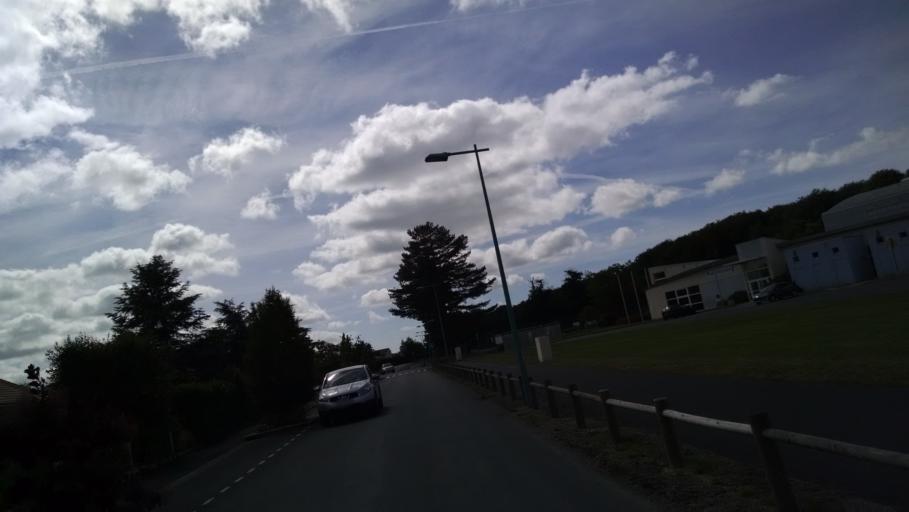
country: FR
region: Pays de la Loire
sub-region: Departement de la Loire-Atlantique
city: Aigrefeuille-sur-Maine
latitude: 47.0755
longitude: -1.4068
